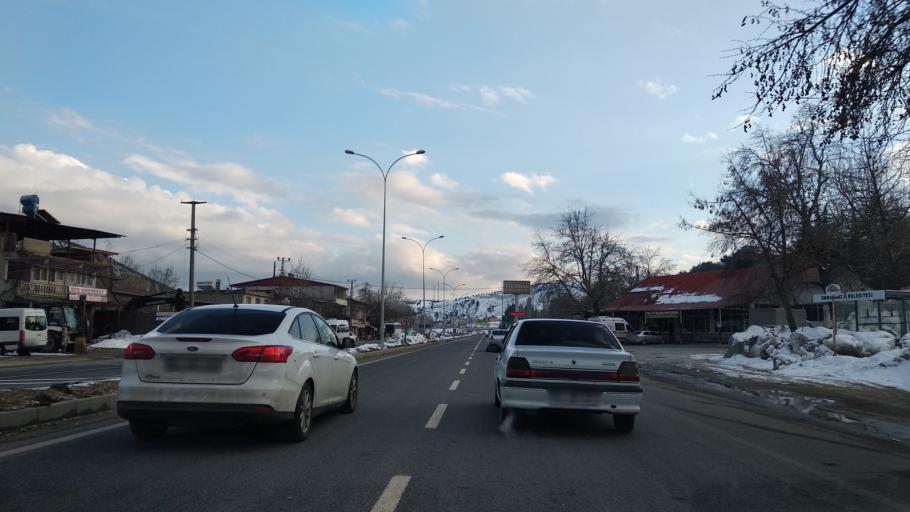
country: TR
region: Kahramanmaras
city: Goksun
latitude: 37.8842
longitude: 36.6241
